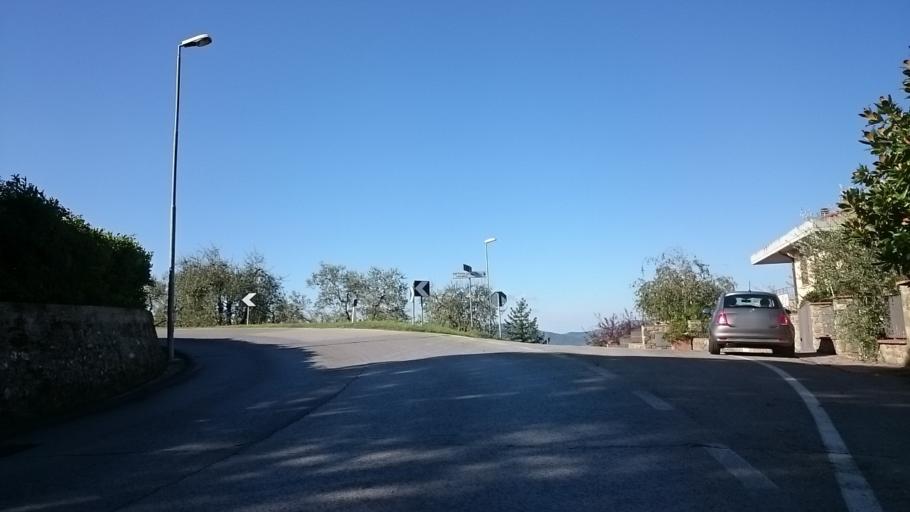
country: IT
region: Tuscany
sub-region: Province of Florence
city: Reggello
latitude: 43.7116
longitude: 11.5179
